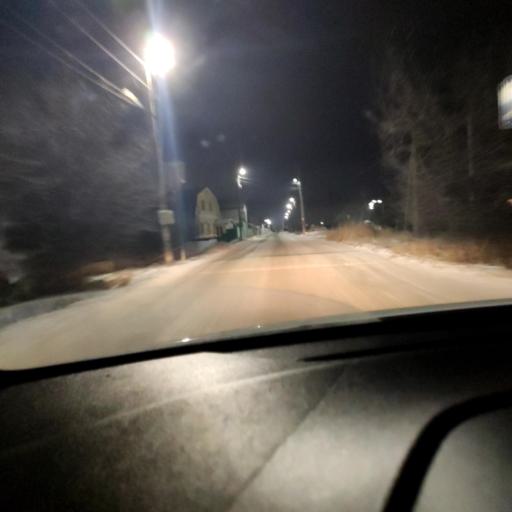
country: RU
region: Tatarstan
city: Staroye Arakchino
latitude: 55.8837
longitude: 49.0398
